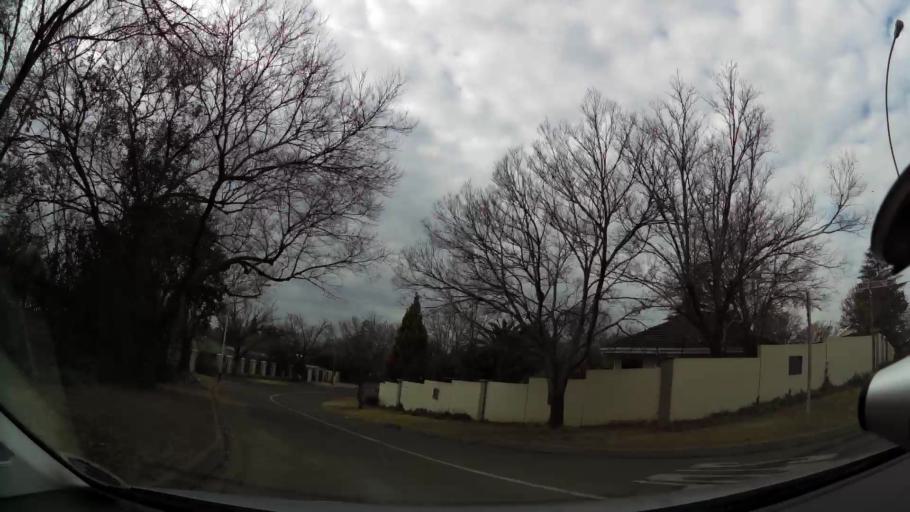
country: ZA
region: Orange Free State
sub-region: Mangaung Metropolitan Municipality
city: Bloemfontein
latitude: -29.0912
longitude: 26.2098
